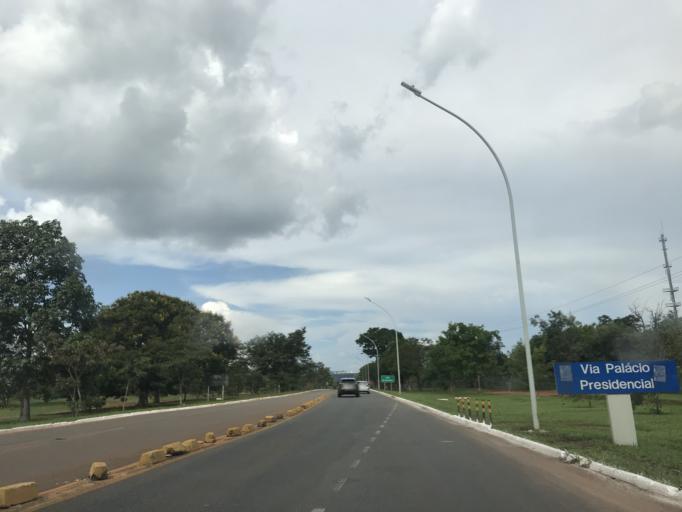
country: BR
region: Federal District
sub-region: Brasilia
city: Brasilia
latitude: -15.8013
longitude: -47.8479
